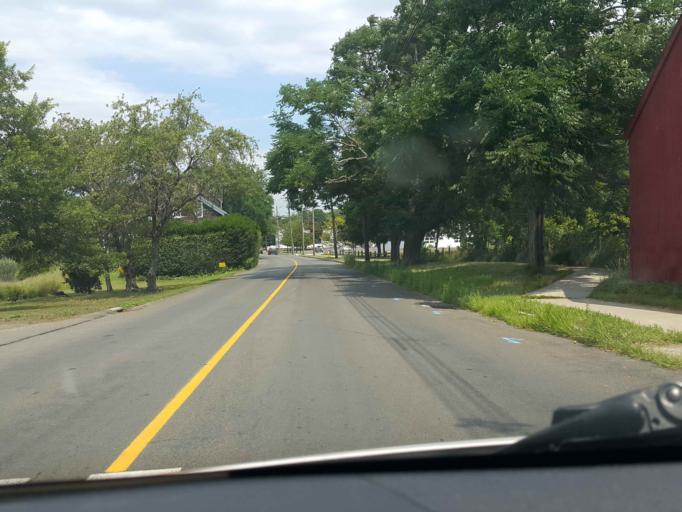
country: US
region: Connecticut
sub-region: New Haven County
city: Guilford
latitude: 41.2846
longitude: -72.6874
